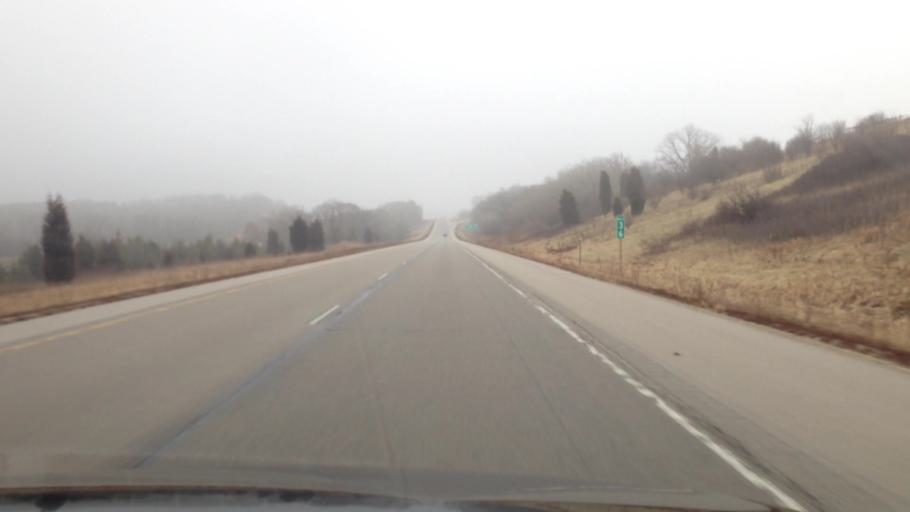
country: US
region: Wisconsin
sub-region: Walworth County
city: East Troy
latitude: 42.7689
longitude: -88.4196
